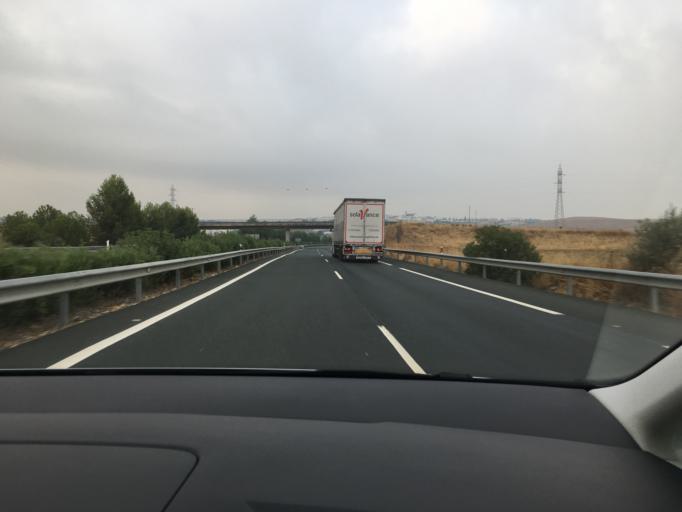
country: ES
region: Andalusia
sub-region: Province of Cordoba
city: La Carlota
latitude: 37.6872
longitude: -4.9235
